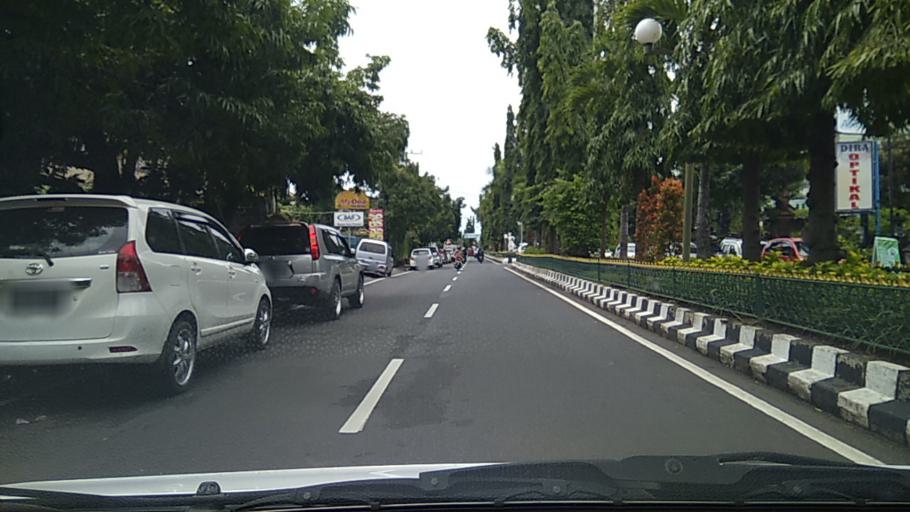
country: ID
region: Bali
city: Banjar Kelodan
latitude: -8.5381
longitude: 115.3228
